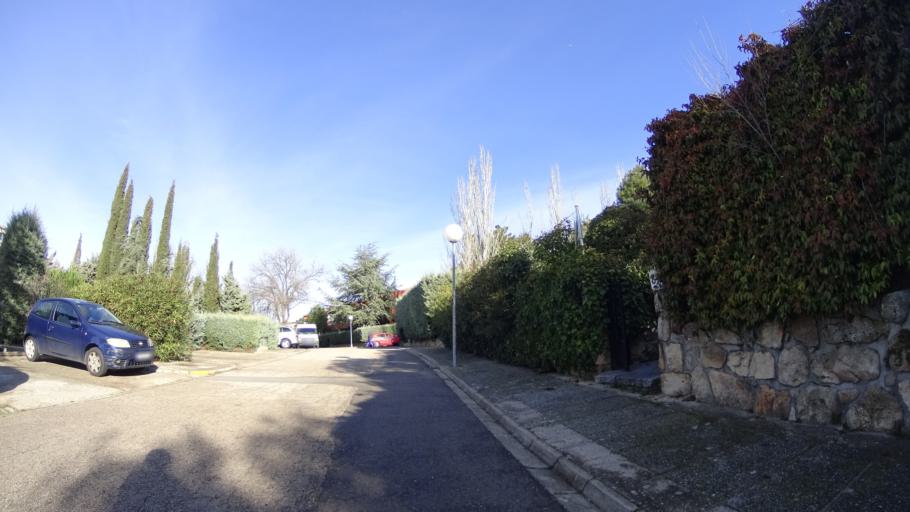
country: ES
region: Madrid
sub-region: Provincia de Madrid
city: Torrelodones
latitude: 40.6088
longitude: -3.9430
